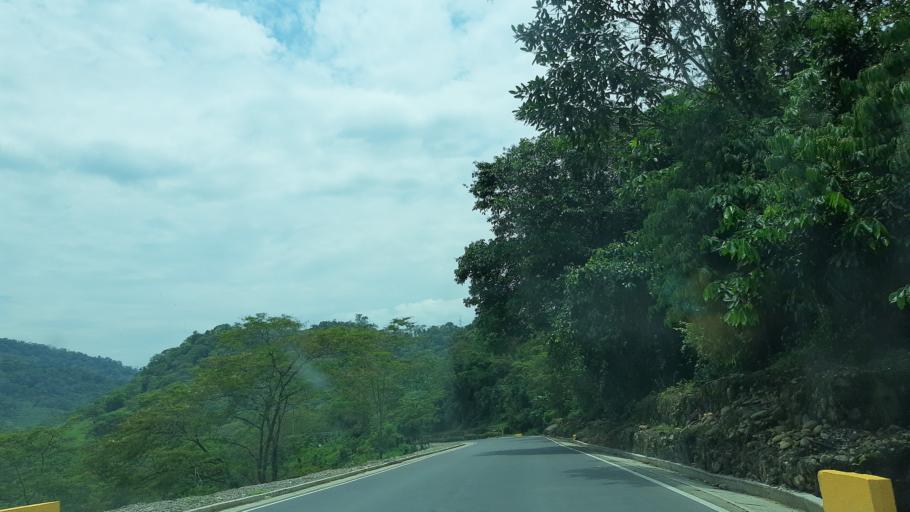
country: CO
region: Casanare
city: Sabanalarga
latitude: 4.8265
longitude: -73.0875
